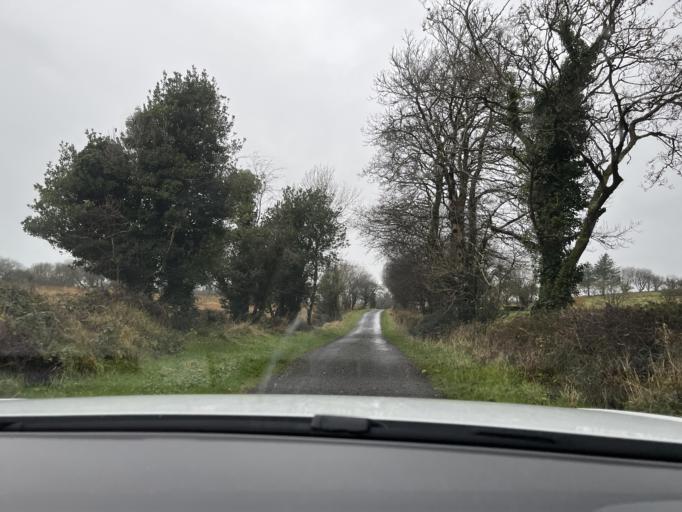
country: IE
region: Connaught
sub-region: County Leitrim
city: Manorhamilton
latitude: 54.2819
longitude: -8.1008
